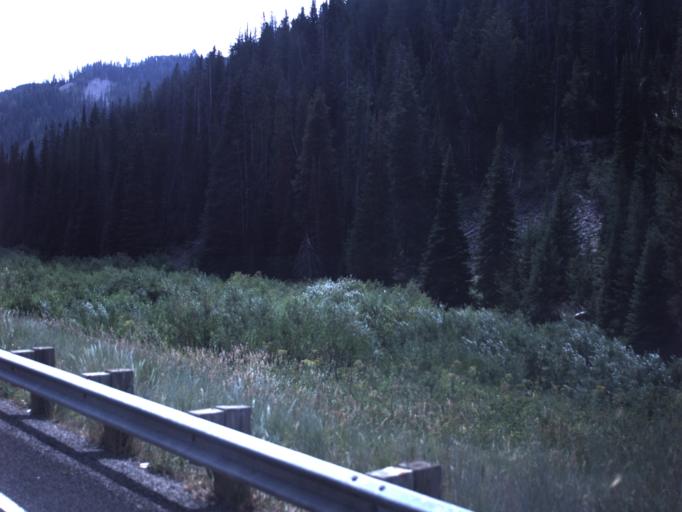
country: US
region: Utah
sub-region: Summit County
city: Francis
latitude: 40.5304
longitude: -111.0963
